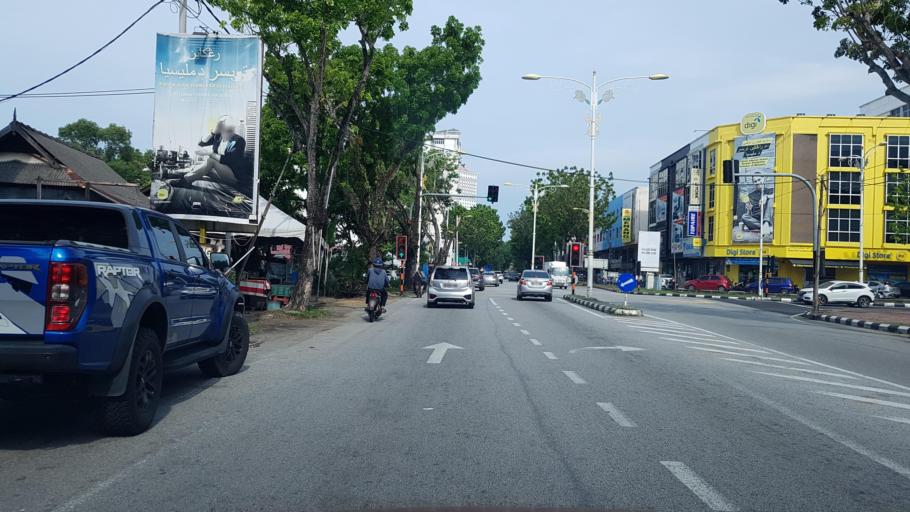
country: MY
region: Terengganu
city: Kuala Terengganu
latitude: 5.3322
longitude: 103.1430
